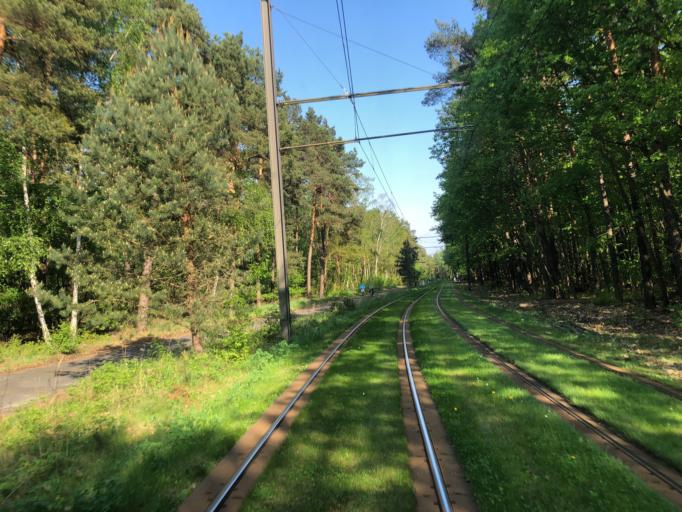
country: DE
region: Berlin
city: Grunau
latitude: 52.4065
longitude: 13.6182
